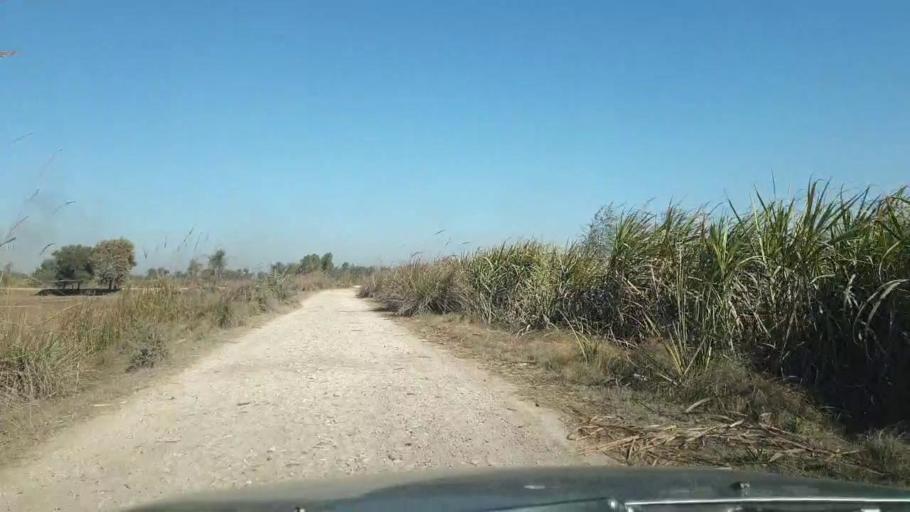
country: PK
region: Sindh
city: Ghotki
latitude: 28.0298
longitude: 69.2880
